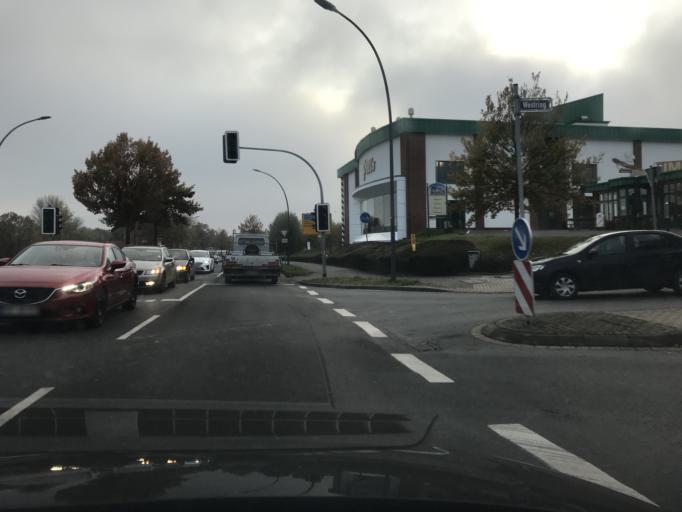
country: DE
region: North Rhine-Westphalia
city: Oelde
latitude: 51.8113
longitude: 8.1338
